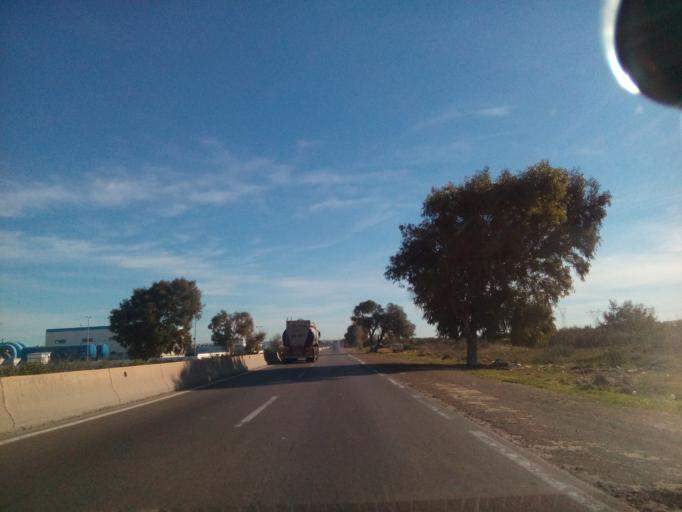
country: DZ
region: Oran
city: Ain el Bya
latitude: 35.7842
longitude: -0.1475
